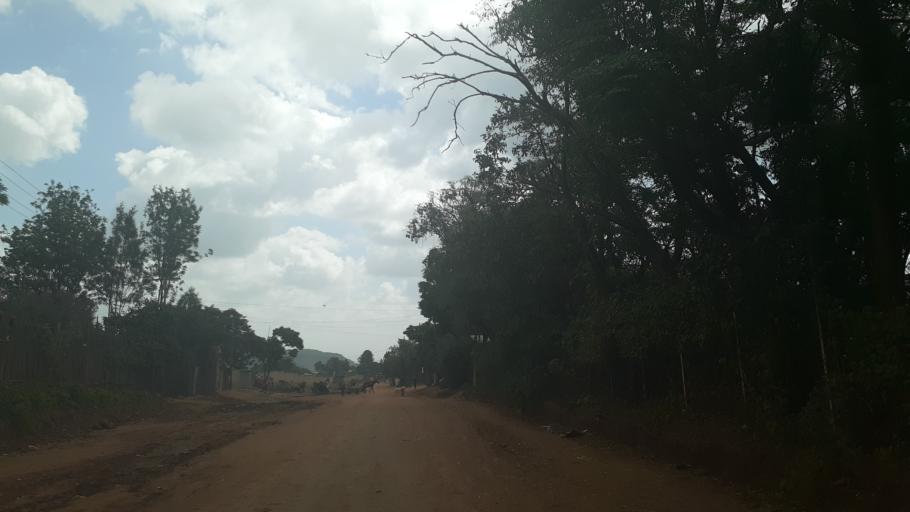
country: ET
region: Oromiya
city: Yabelo
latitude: 4.8961
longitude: 38.0946
